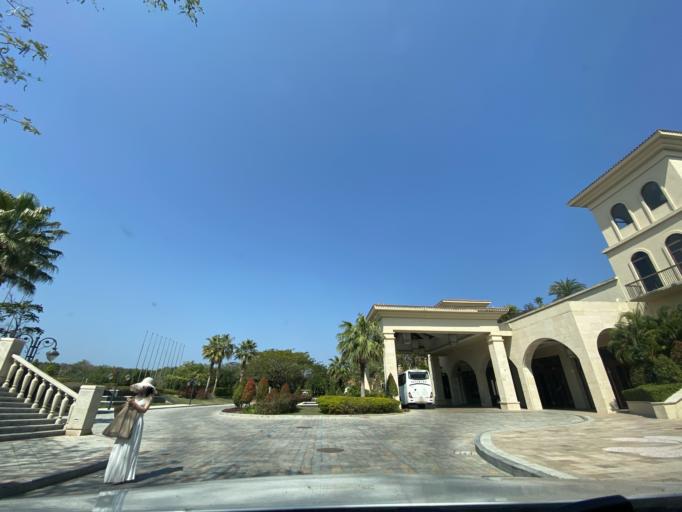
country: CN
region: Hainan
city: Haitangwan
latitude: 18.3493
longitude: 109.7356
